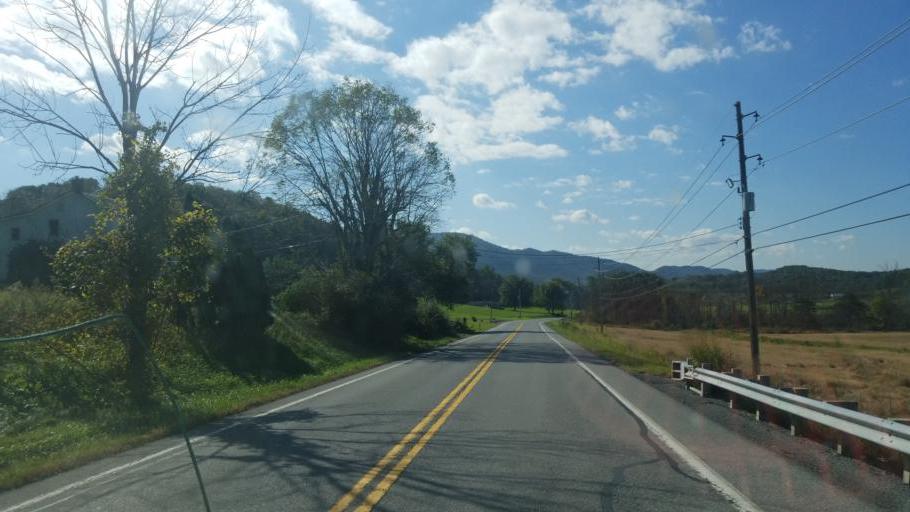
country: US
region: Pennsylvania
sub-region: Bedford County
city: Bedford
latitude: 40.0623
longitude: -78.5516
